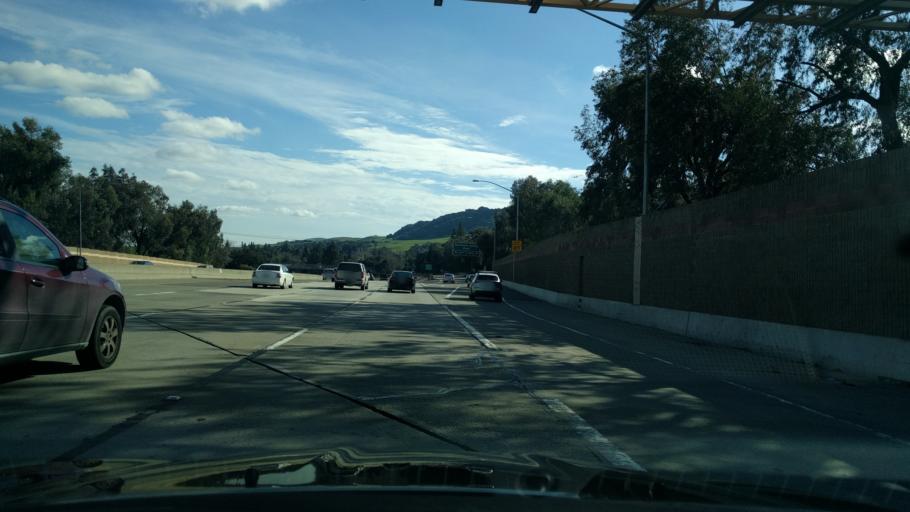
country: US
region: California
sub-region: Contra Costa County
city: Danville
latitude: 37.8154
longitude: -121.9935
